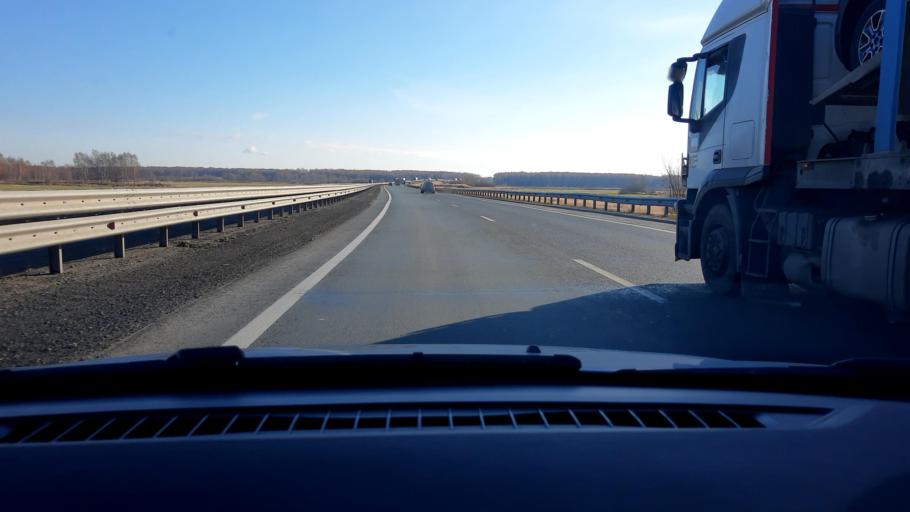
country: RU
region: Nizjnij Novgorod
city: Burevestnik
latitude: 56.1252
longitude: 43.7917
